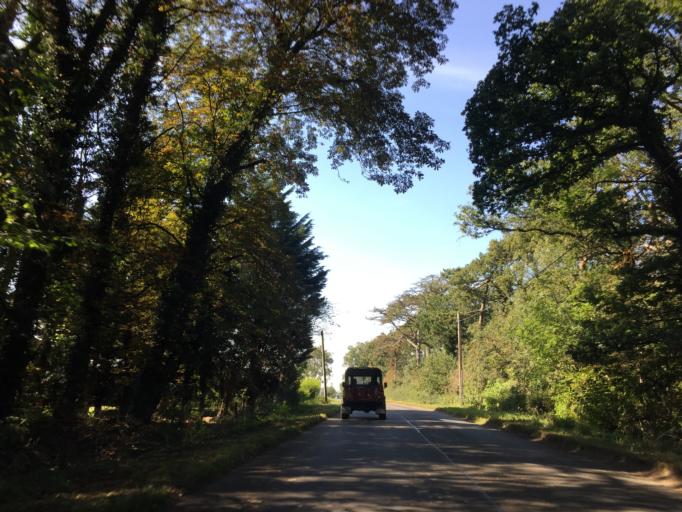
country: GB
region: England
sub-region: Leicestershire
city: Queniborough
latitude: 52.6972
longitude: -1.0006
